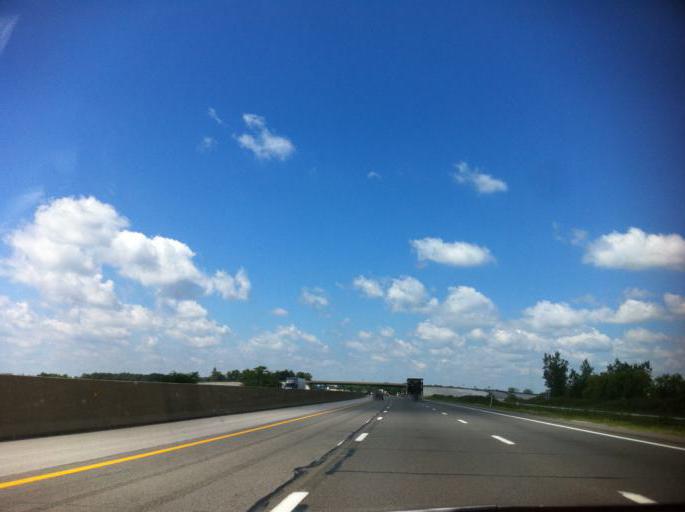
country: US
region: Ohio
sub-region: Sandusky County
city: Clyde
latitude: 41.3787
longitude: -82.9981
